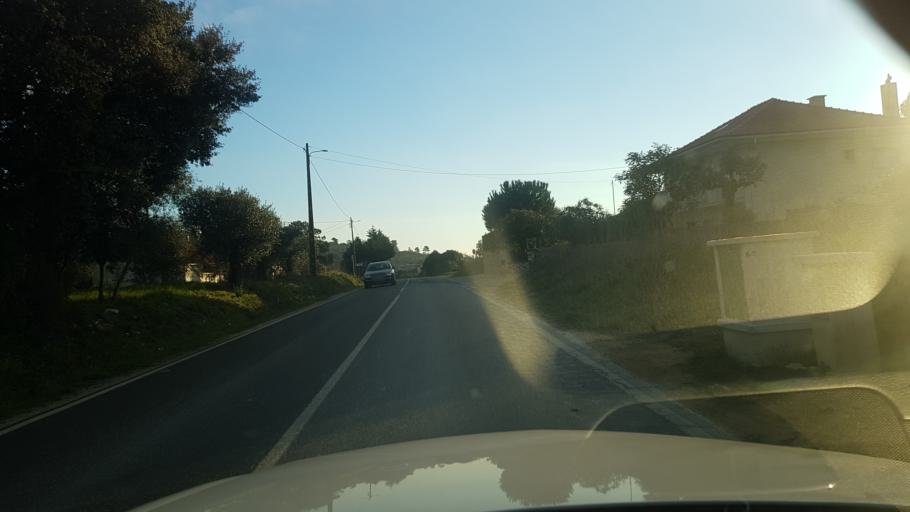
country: PT
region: Santarem
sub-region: Ourem
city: Ourem
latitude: 39.5725
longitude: -8.5927
